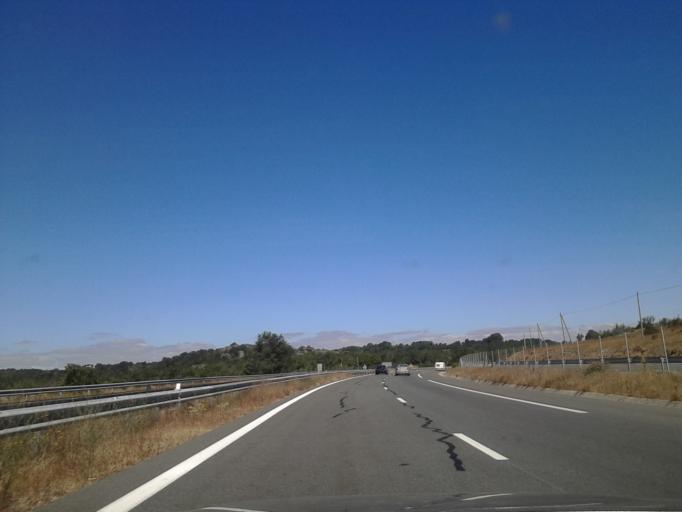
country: FR
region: Midi-Pyrenees
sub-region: Departement de l'Aveyron
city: La Cavalerie
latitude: 43.8907
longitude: 3.2847
